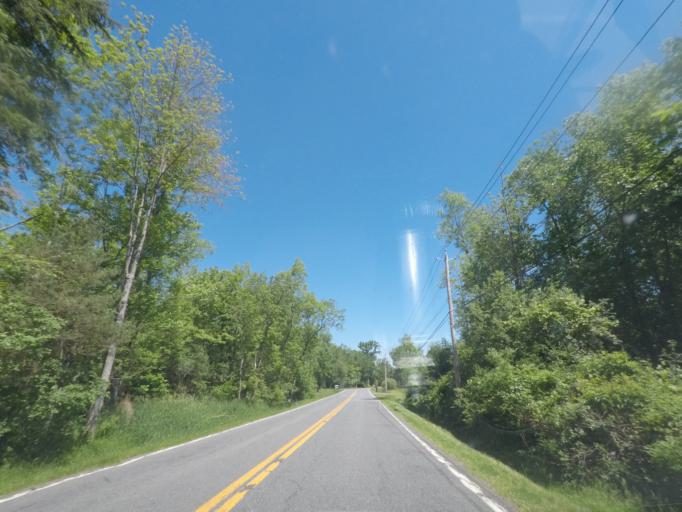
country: US
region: New York
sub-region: Schenectady County
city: East Glenville
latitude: 42.8813
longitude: -73.8651
